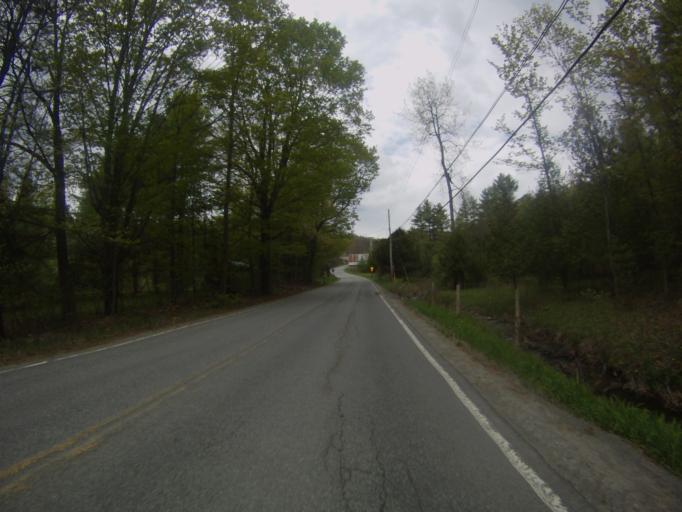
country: US
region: New York
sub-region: Essex County
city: Port Henry
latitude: 43.9584
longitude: -73.4876
